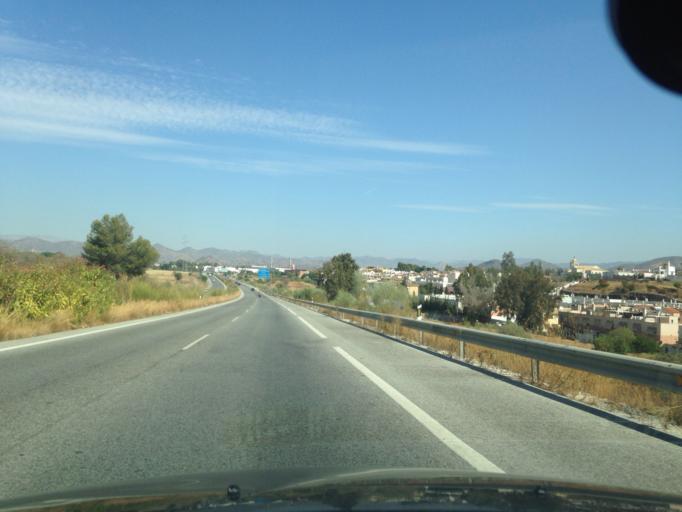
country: ES
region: Andalusia
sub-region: Provincia de Malaga
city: Alhaurin de la Torre
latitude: 36.7232
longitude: -4.5534
